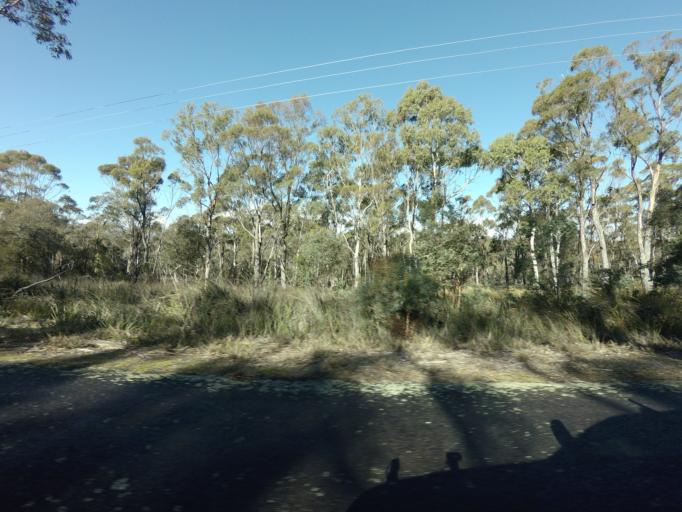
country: AU
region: Tasmania
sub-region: Sorell
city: Sorell
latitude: -42.3612
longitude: 147.9553
